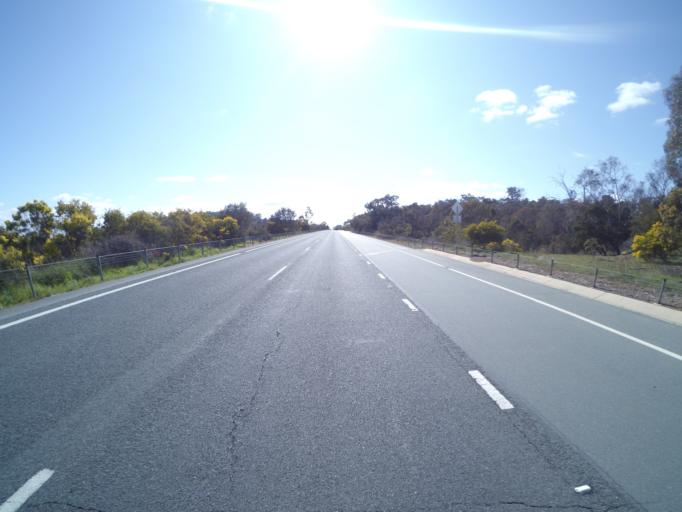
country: AU
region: Australian Capital Territory
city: Kaleen
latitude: -35.2181
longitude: 149.1817
